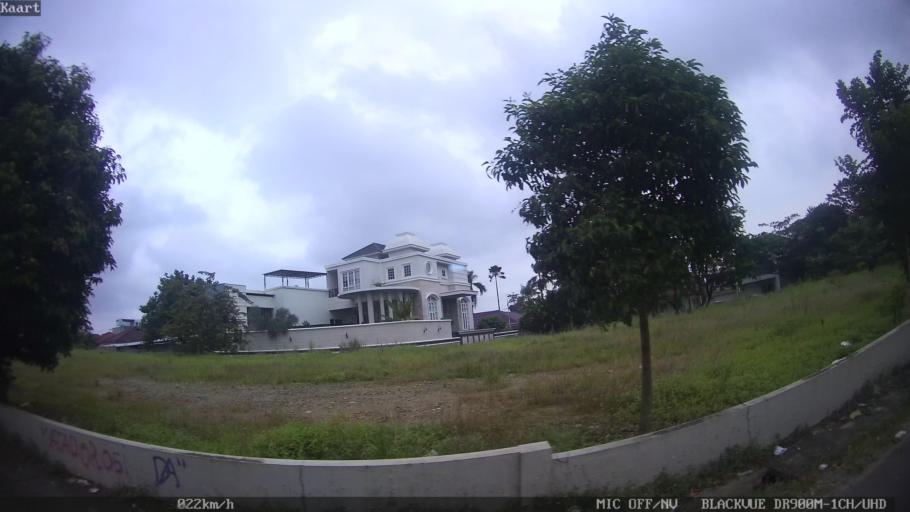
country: ID
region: Lampung
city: Bandarlampung
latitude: -5.4126
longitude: 105.2760
